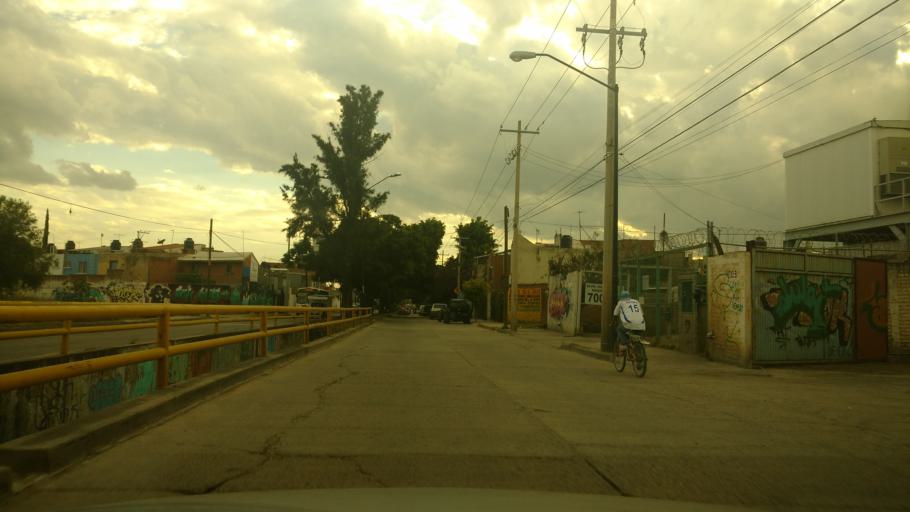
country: MX
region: Guanajuato
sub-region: Leon
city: Medina
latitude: 21.1565
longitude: -101.6447
